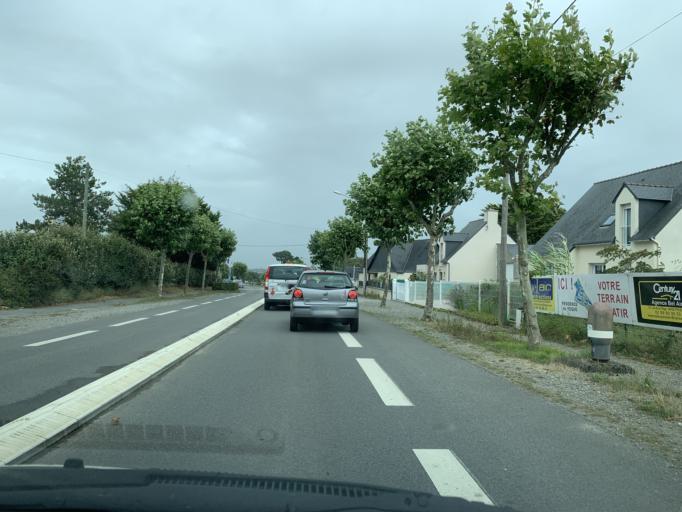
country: FR
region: Brittany
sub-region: Departement du Morbihan
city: Penestin
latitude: 47.4796
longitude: -2.4750
